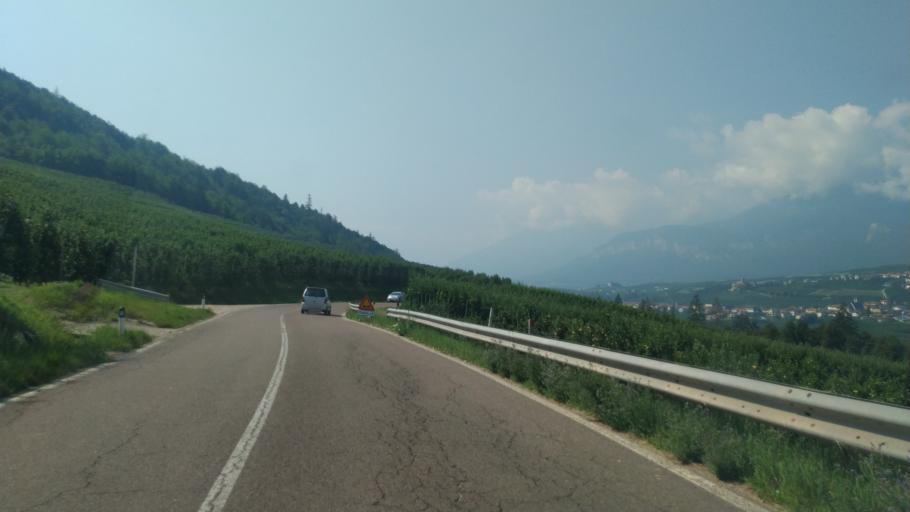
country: IT
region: Trentino-Alto Adige
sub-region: Provincia di Trento
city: Sanzeno
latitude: 46.3491
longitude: 11.0653
